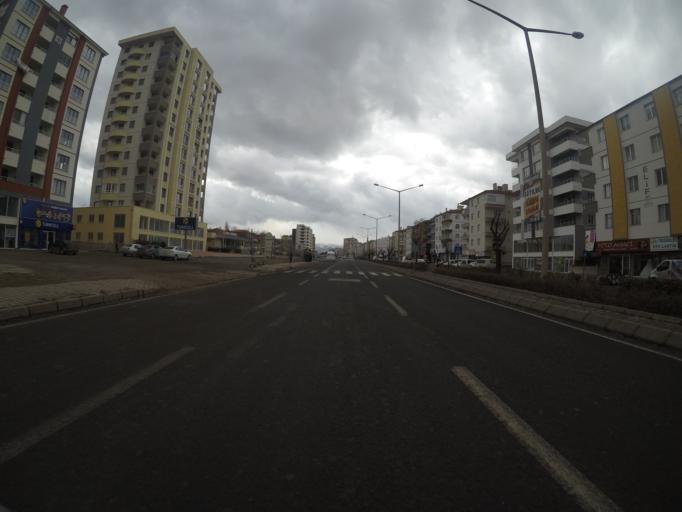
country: TR
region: Kayseri
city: Melikgazi
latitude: 38.7573
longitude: 35.4672
